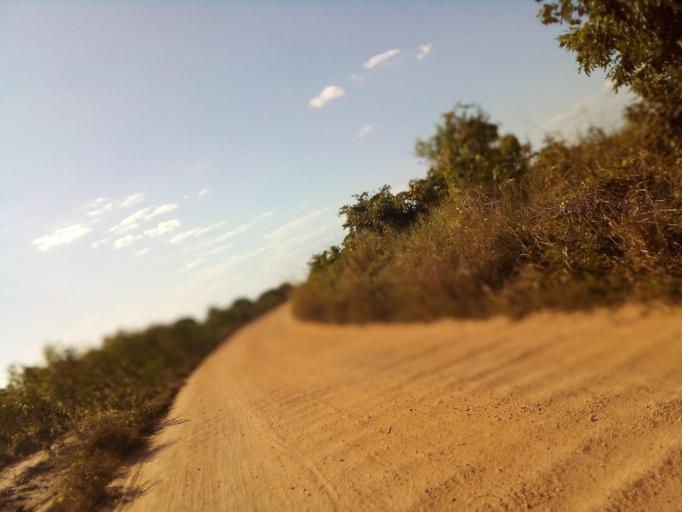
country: MZ
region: Zambezia
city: Quelimane
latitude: -17.5630
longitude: 36.6359
